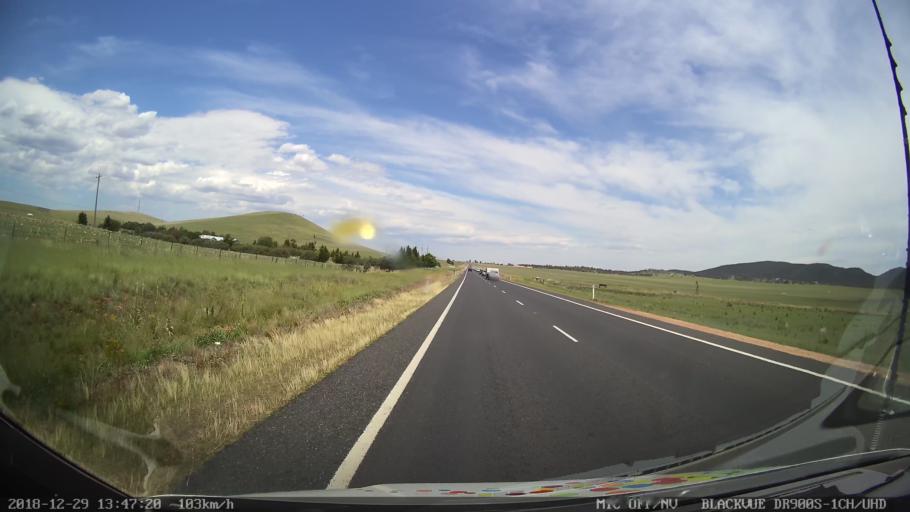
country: AU
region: New South Wales
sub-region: Cooma-Monaro
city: Cooma
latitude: -36.1250
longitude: 149.1424
